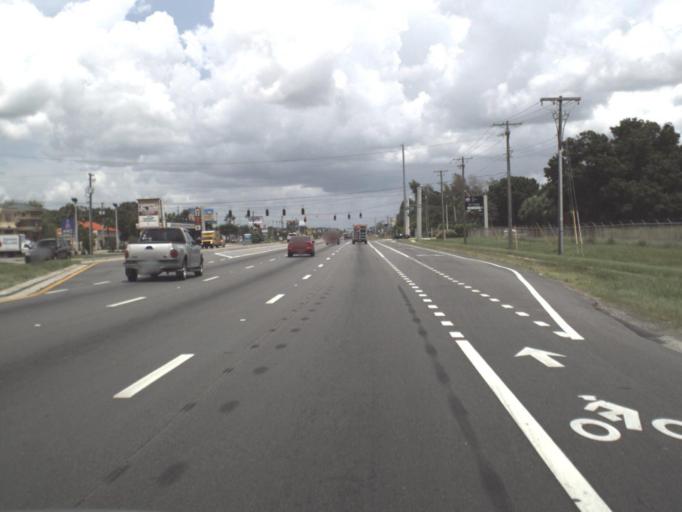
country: US
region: Florida
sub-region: Hillsborough County
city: Egypt Lake-Leto
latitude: 27.9961
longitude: -82.5260
